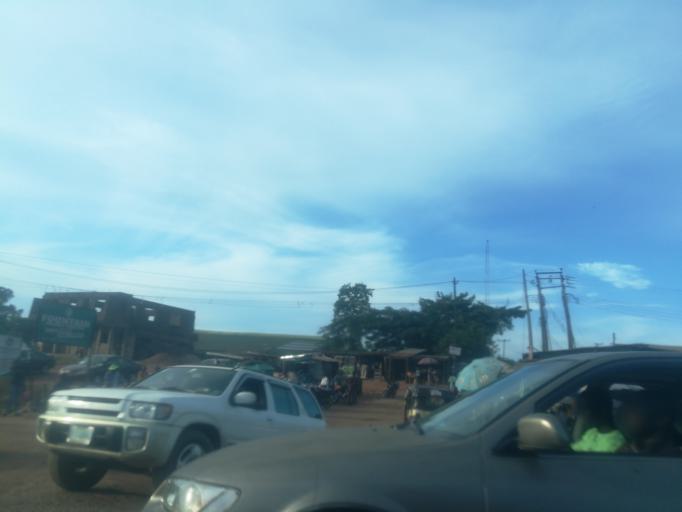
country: NG
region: Oyo
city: Ibadan
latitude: 7.3384
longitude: 3.9008
